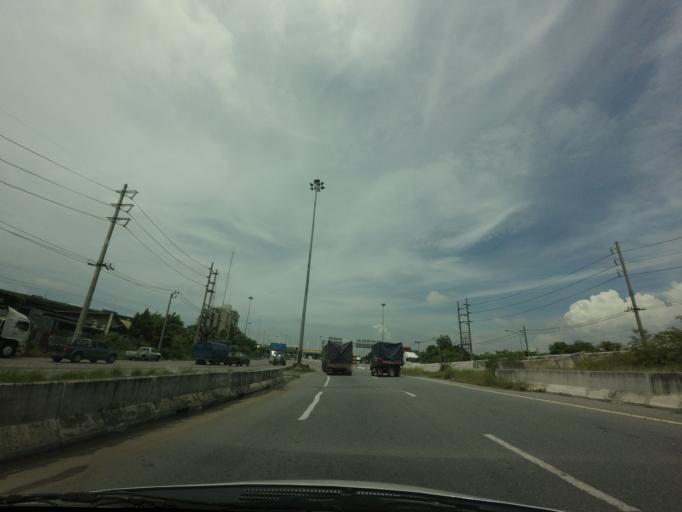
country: TH
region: Bangkok
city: Thung Khru
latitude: 13.6319
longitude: 100.5280
